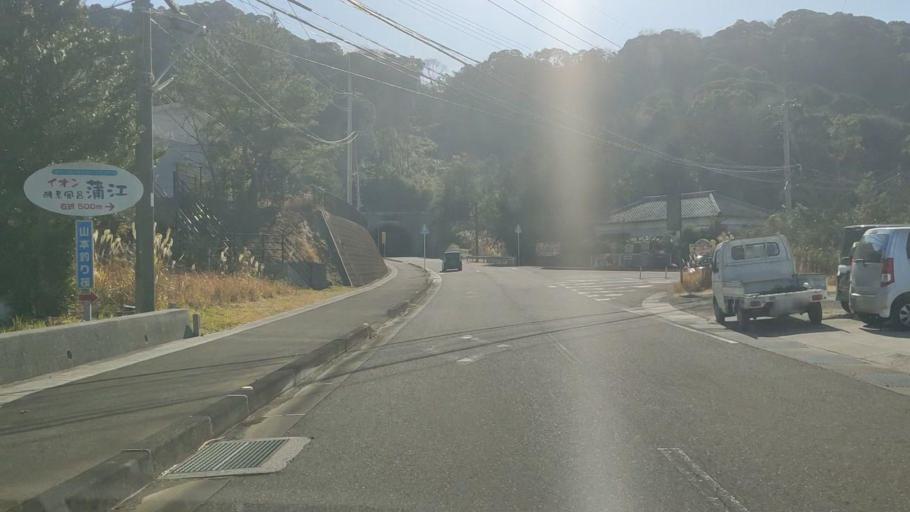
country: JP
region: Oita
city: Saiki
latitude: 32.7991
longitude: 131.9003
